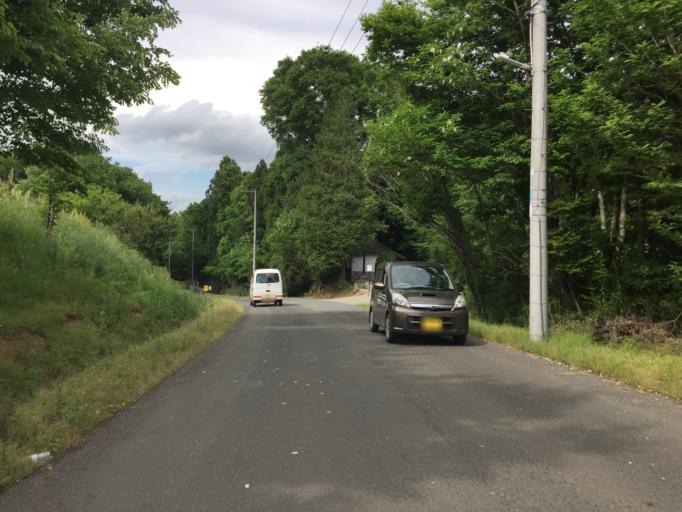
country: JP
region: Fukushima
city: Nihommatsu
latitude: 37.6442
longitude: 140.5263
